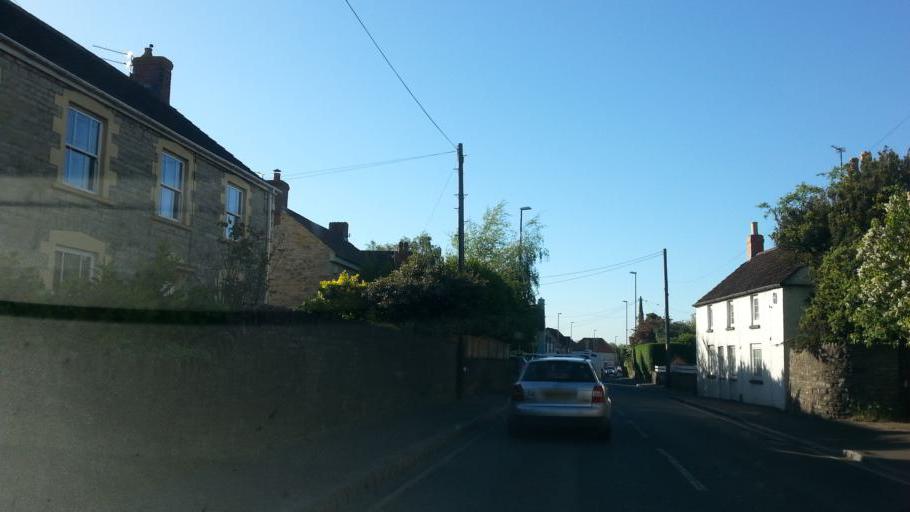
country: GB
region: England
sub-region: Bath and North East Somerset
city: Whitchurch
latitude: 51.4052
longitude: -2.5577
